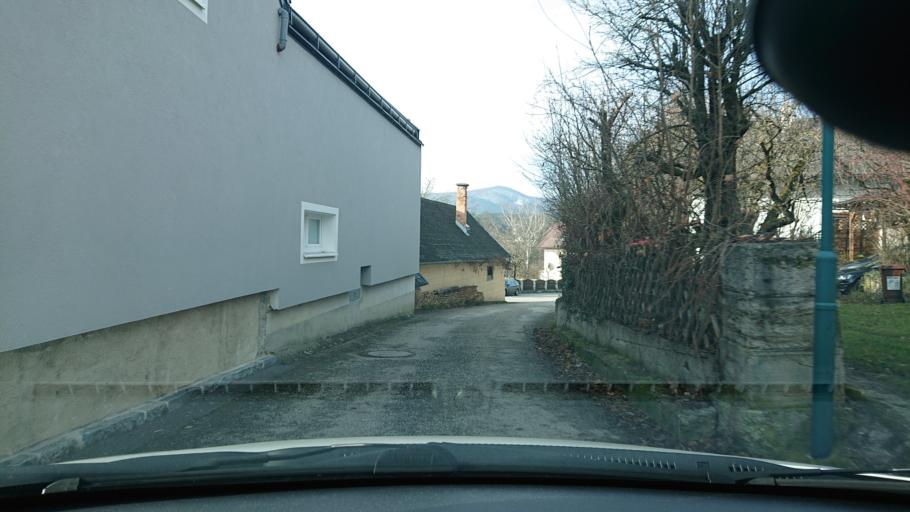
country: AT
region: Lower Austria
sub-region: Politischer Bezirk Baden
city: Hernstein
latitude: 47.8955
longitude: 16.1056
